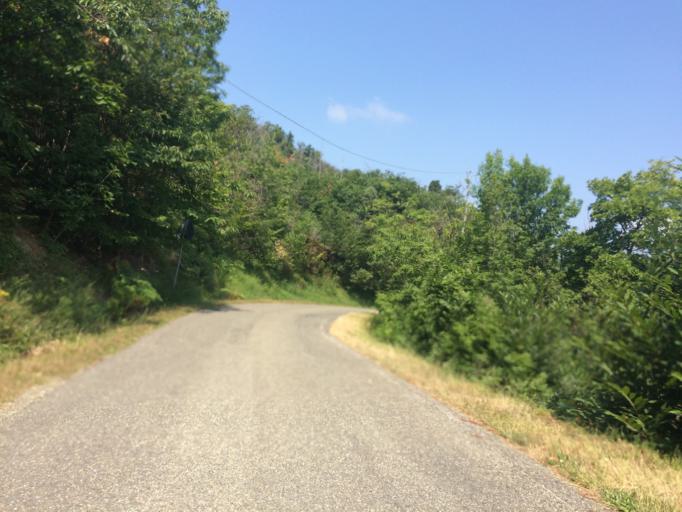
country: IT
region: Piedmont
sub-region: Provincia di Alessandria
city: Malvicino
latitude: 44.5373
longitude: 8.4119
